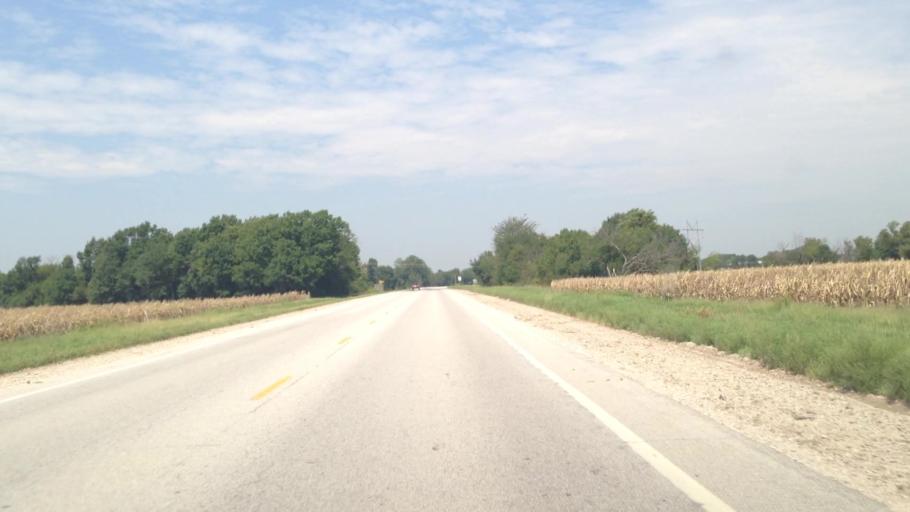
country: US
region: Kansas
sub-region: Labette County
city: Parsons
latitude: 37.3867
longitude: -95.2656
